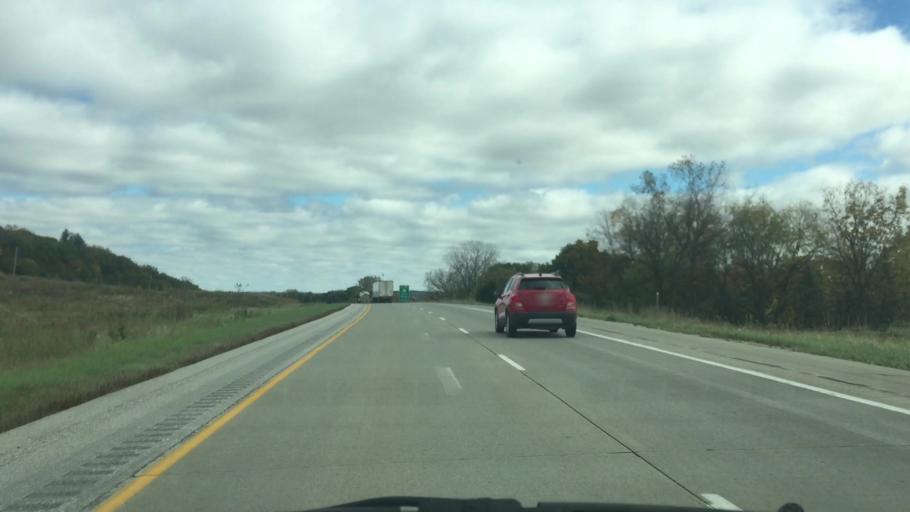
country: US
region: Iowa
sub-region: Jasper County
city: Colfax
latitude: 41.6858
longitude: -93.2775
